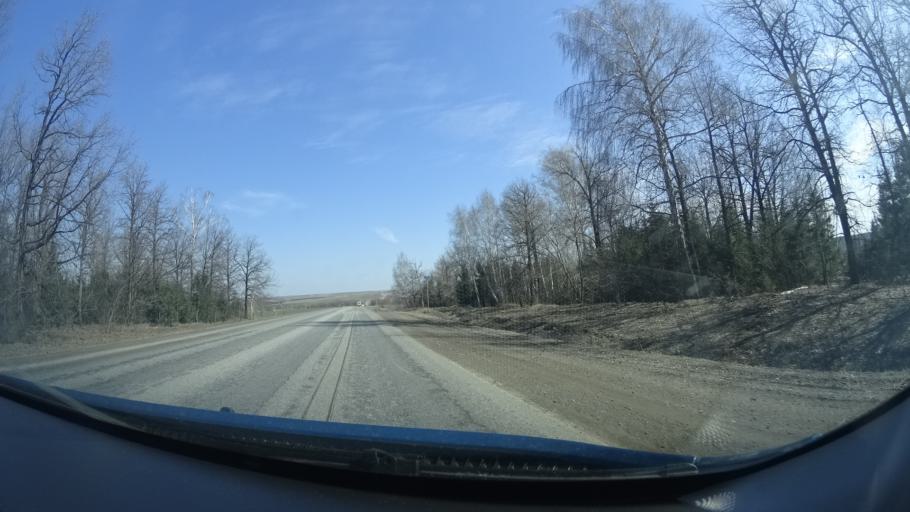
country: RU
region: Bashkortostan
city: Nizhnetroitskiy
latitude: 54.4531
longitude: 53.6462
